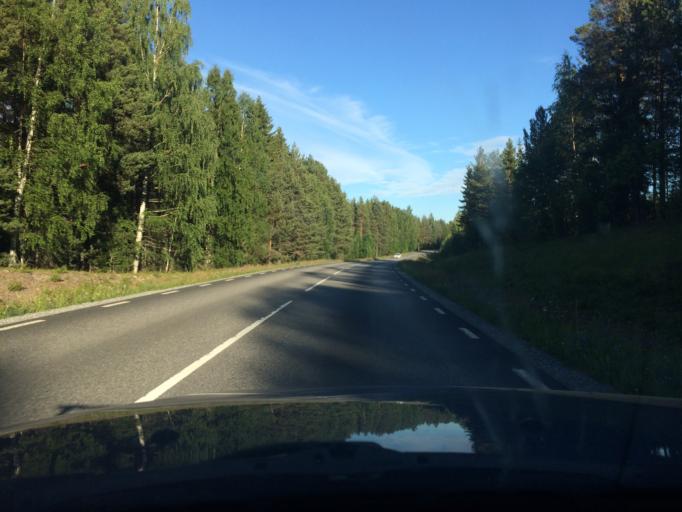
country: SE
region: Norrbotten
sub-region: Pitea Kommun
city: Roknas
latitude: 65.3316
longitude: 21.2067
